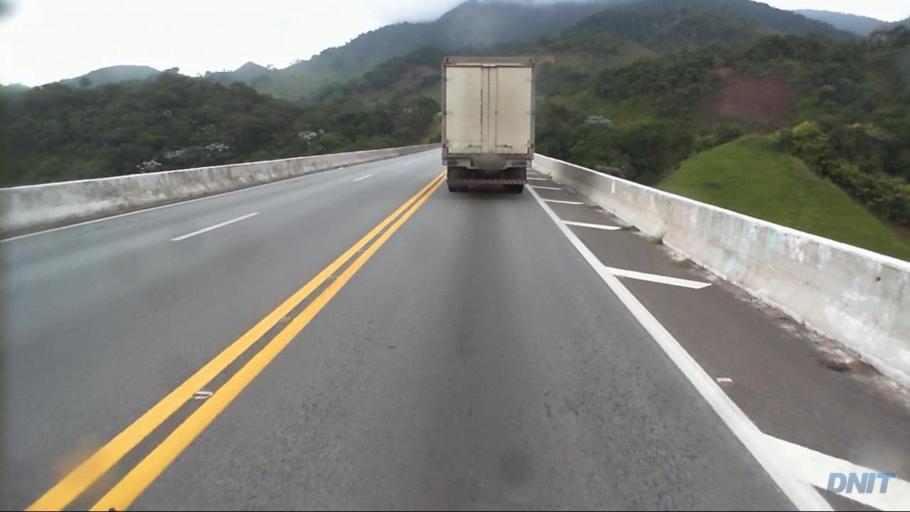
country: BR
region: Minas Gerais
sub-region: Nova Era
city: Nova Era
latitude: -19.6548
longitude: -42.9552
